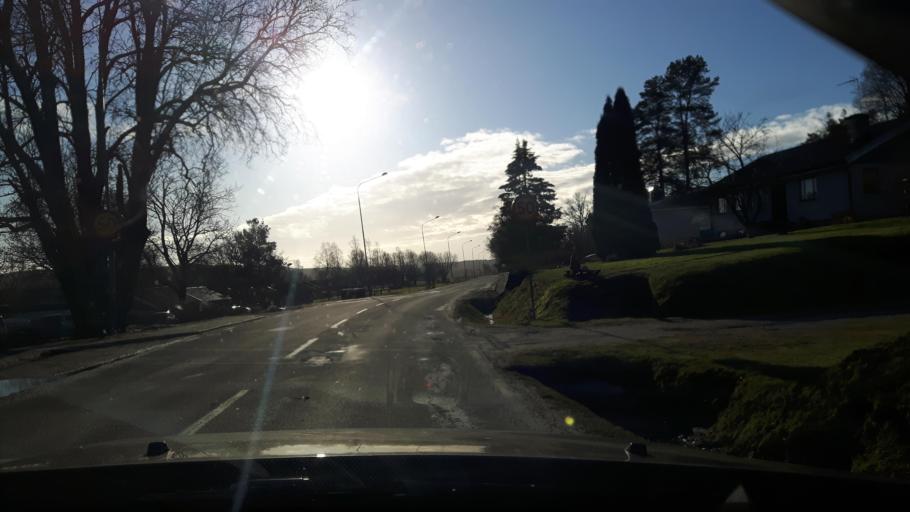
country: SE
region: Vaestra Goetaland
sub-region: Munkedals Kommun
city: Munkedal
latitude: 58.6442
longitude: 11.7799
